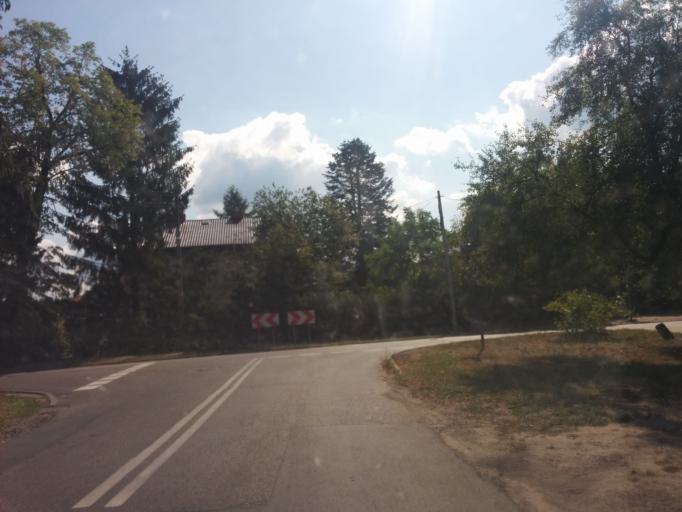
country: PL
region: Masovian Voivodeship
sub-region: Warszawa
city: Bialoleka
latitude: 52.3409
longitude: 20.9863
